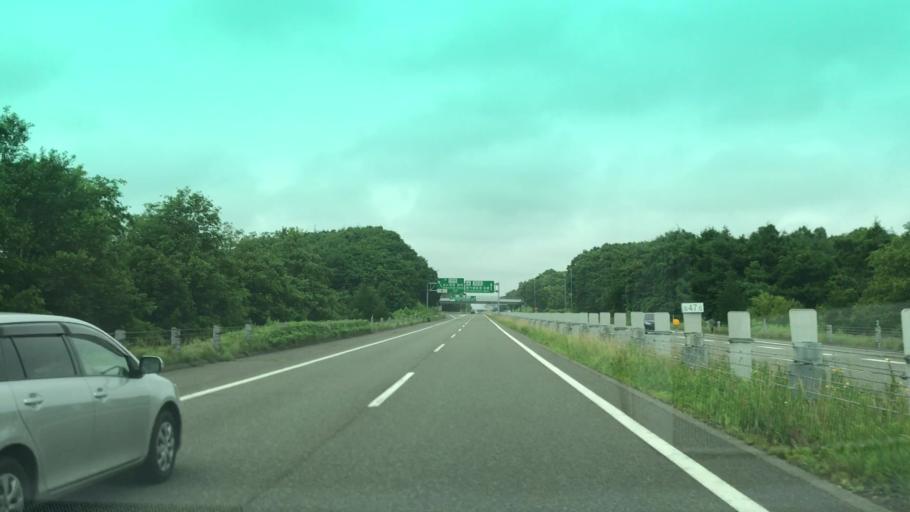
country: JP
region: Hokkaido
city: Tomakomai
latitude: 42.7077
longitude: 141.6518
